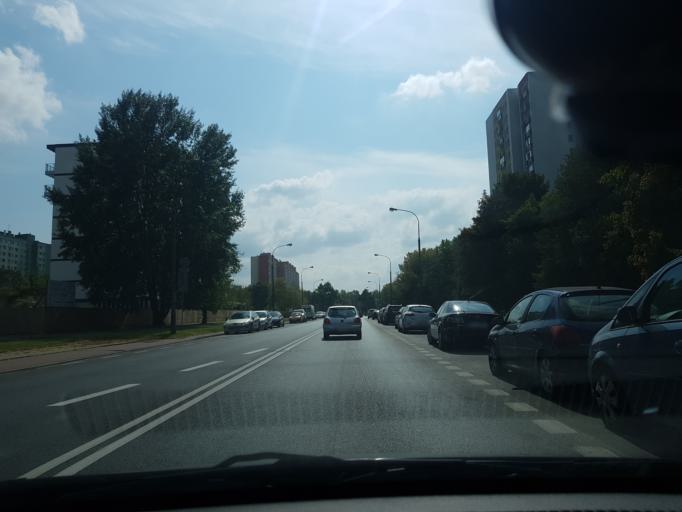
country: PL
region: Masovian Voivodeship
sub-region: Warszawa
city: Bielany
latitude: 52.2789
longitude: 20.9230
